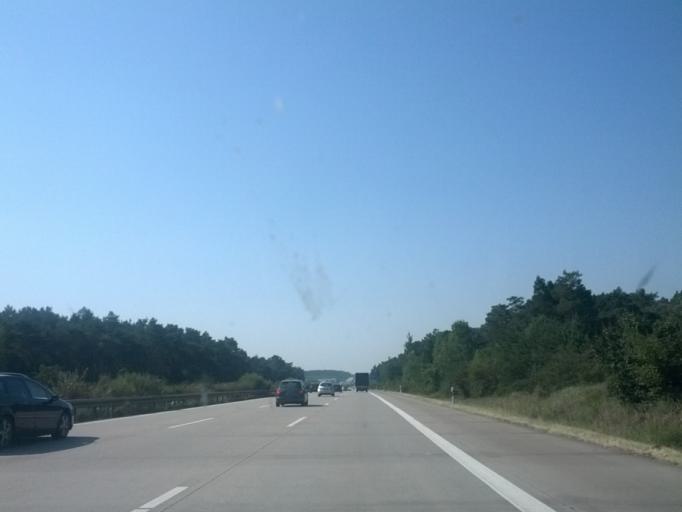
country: DE
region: Brandenburg
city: Linthe
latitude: 52.1430
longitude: 12.7639
